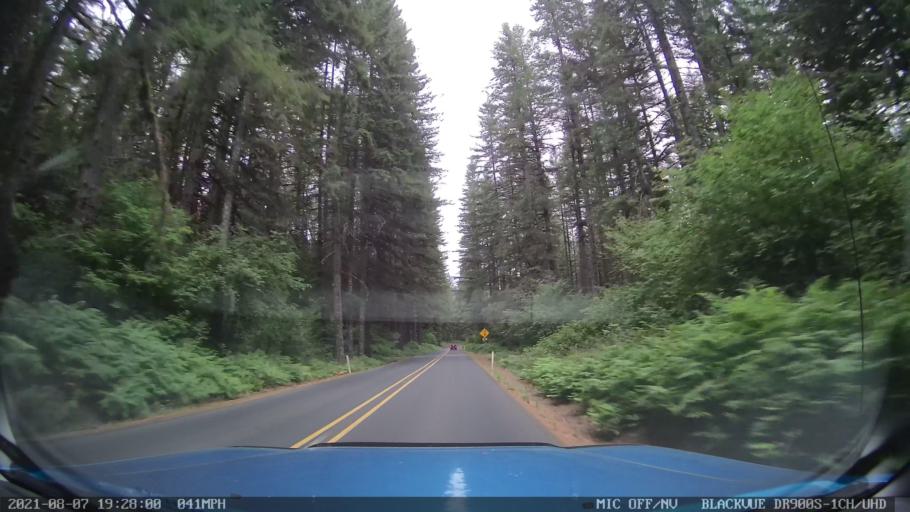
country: US
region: Oregon
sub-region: Linn County
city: Lyons
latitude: 44.8810
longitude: -122.6413
